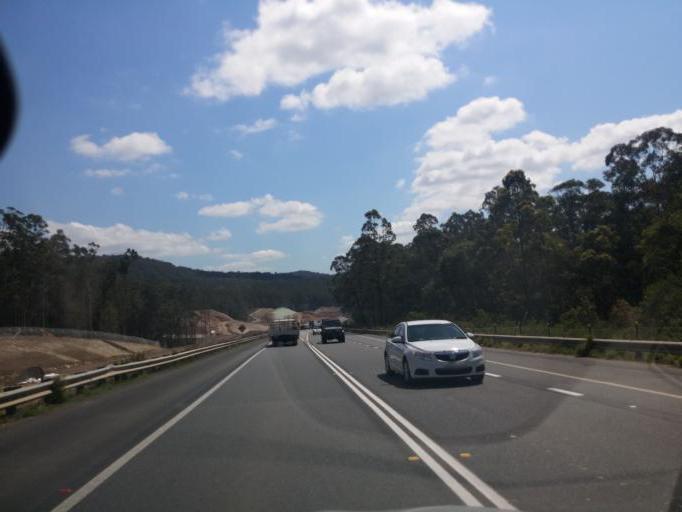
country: AU
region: New South Wales
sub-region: Port Macquarie-Hastings
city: North Shore
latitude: -31.2791
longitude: 152.8132
